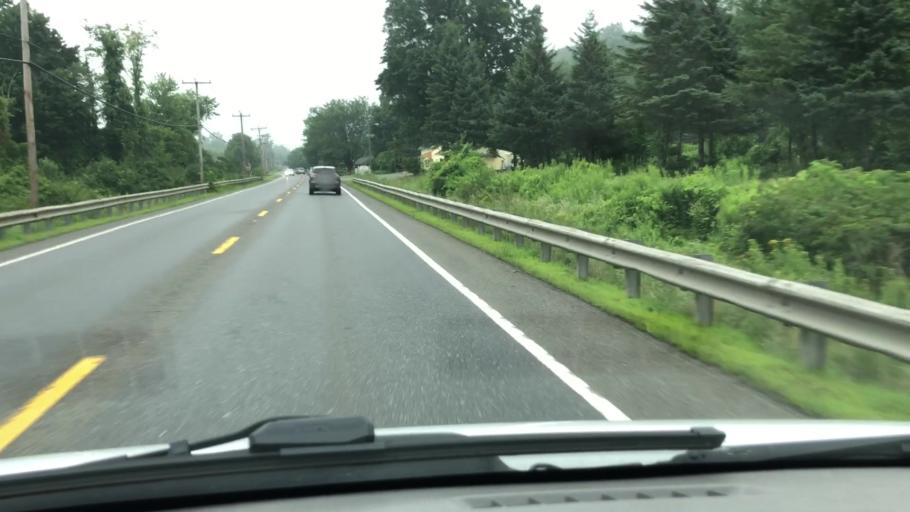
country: US
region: Massachusetts
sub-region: Franklin County
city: Greenfield
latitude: 42.5326
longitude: -72.6037
